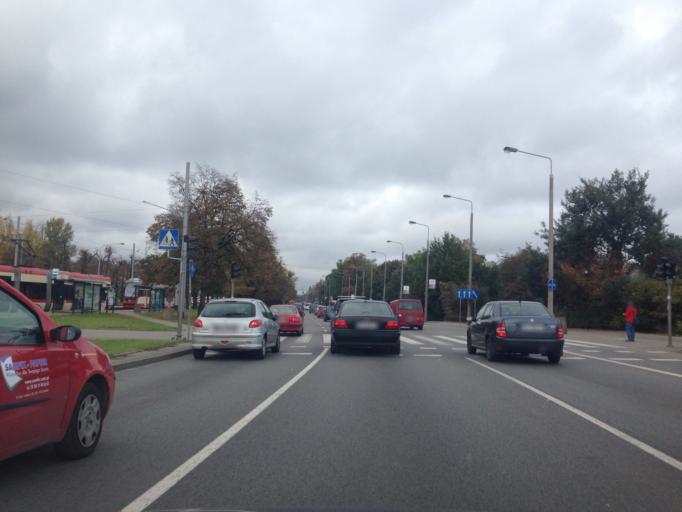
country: PL
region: Pomeranian Voivodeship
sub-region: Gdansk
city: Gdansk
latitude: 54.3618
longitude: 18.6424
